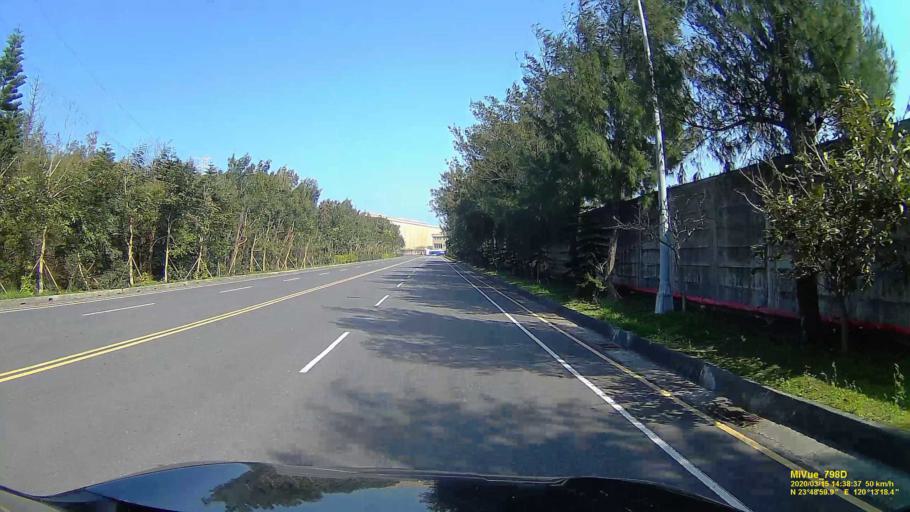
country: TW
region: Taiwan
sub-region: Yunlin
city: Douliu
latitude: 23.8166
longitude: 120.2221
